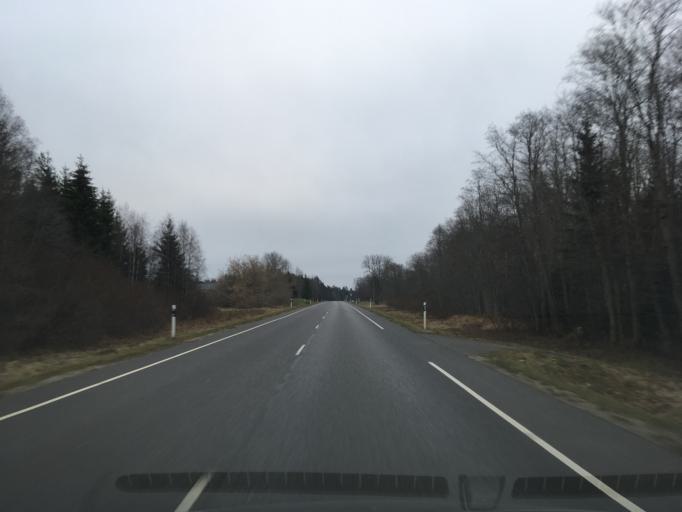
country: EE
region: Laeaene-Virumaa
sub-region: Tapa vald
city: Tapa
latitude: 59.4574
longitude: 25.9868
